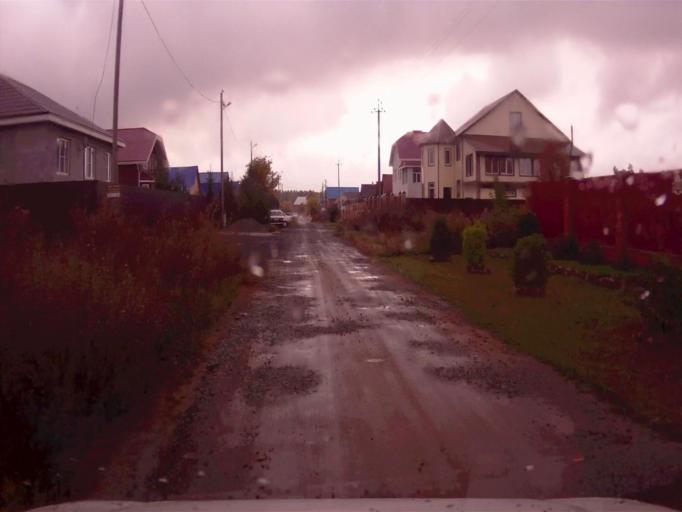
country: RU
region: Chelyabinsk
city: Dolgoderevenskoye
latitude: 55.3072
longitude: 61.3414
